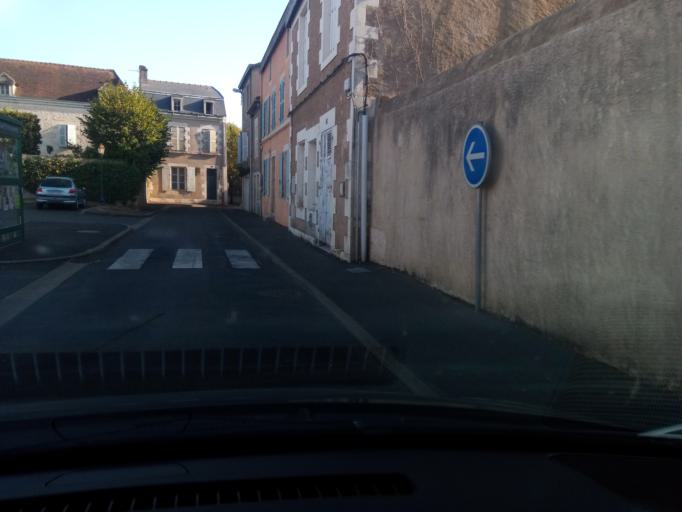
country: FR
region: Poitou-Charentes
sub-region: Departement de la Vienne
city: Montmorillon
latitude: 46.4247
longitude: 0.8686
